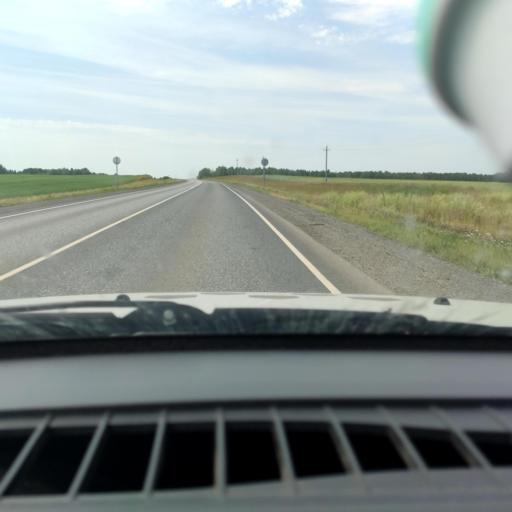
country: RU
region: Perm
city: Siva
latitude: 58.5244
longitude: 53.9973
